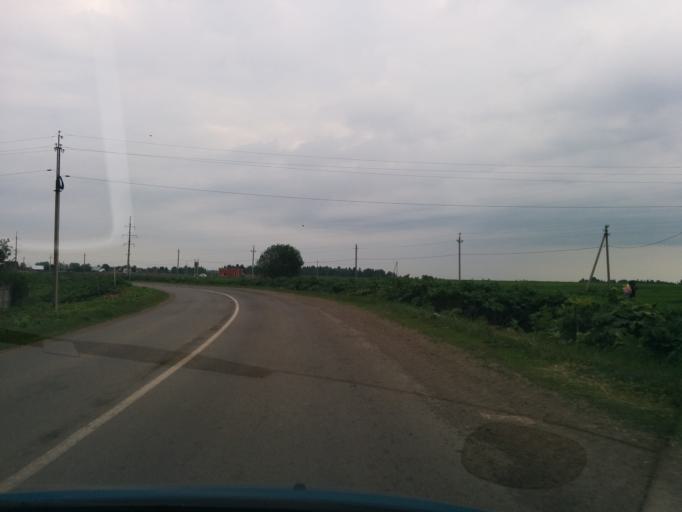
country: RU
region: Perm
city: Polazna
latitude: 58.2217
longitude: 56.2976
